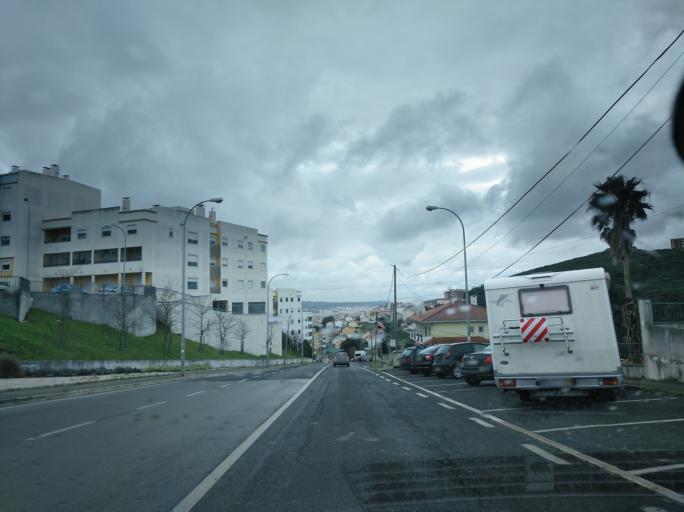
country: PT
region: Lisbon
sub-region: Odivelas
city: Famoes
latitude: 38.7910
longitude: -9.2279
